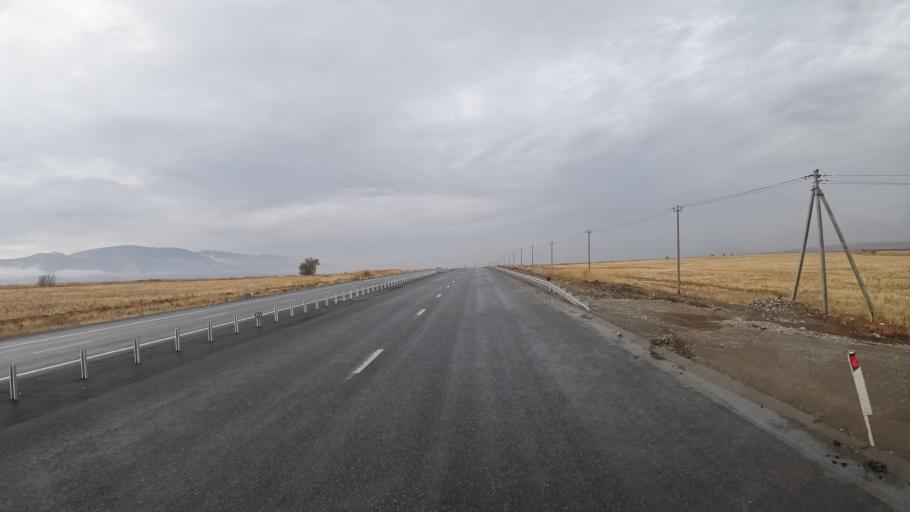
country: KZ
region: Ongtustik Qazaqstan
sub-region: Tulkibas Audany
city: Zhabagly
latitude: 42.5070
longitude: 70.4402
